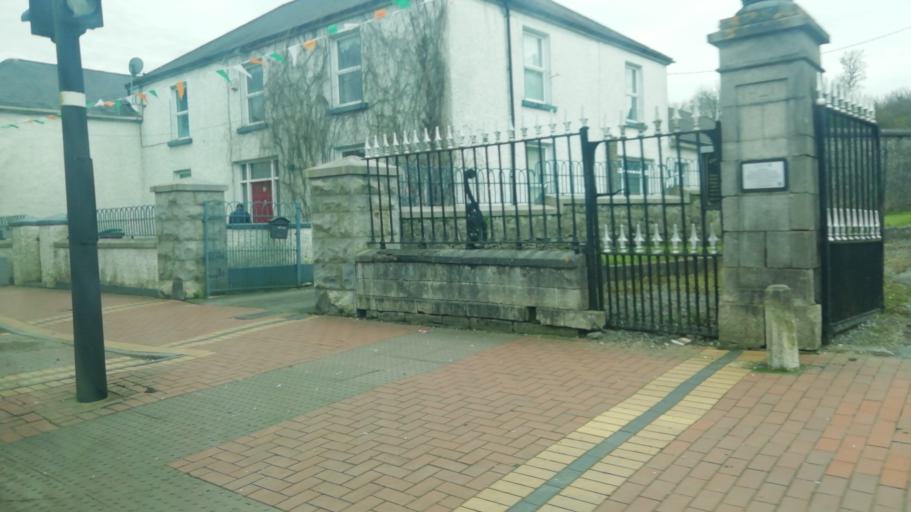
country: IE
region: Leinster
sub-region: Uibh Fhaili
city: Edenderry
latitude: 53.3427
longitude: -7.0530
